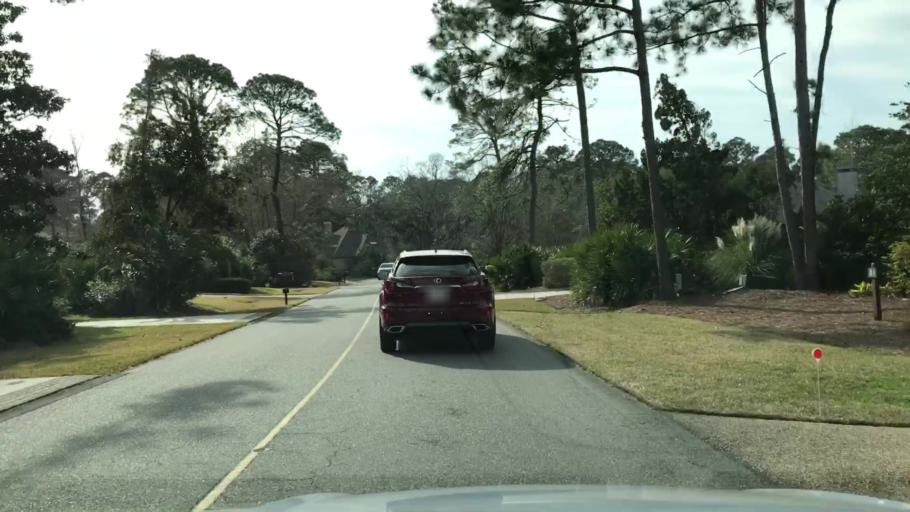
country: US
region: South Carolina
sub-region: Beaufort County
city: Hilton Head Island
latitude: 32.2399
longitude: -80.7123
